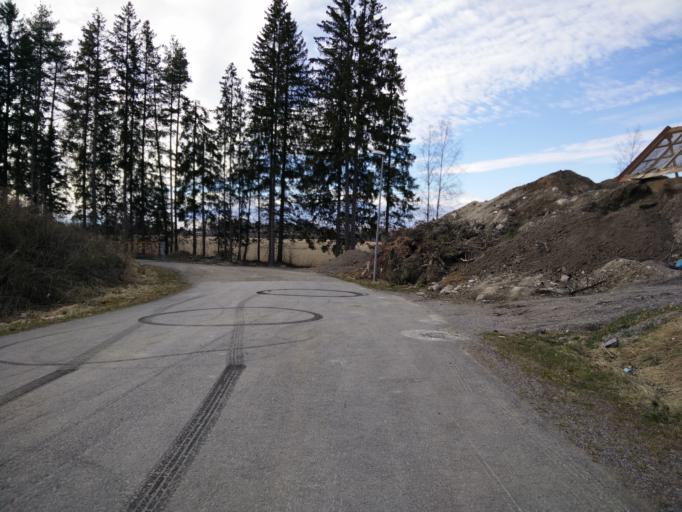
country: FI
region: Pirkanmaa
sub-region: Tampere
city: Orivesi
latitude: 61.6973
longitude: 24.3519
